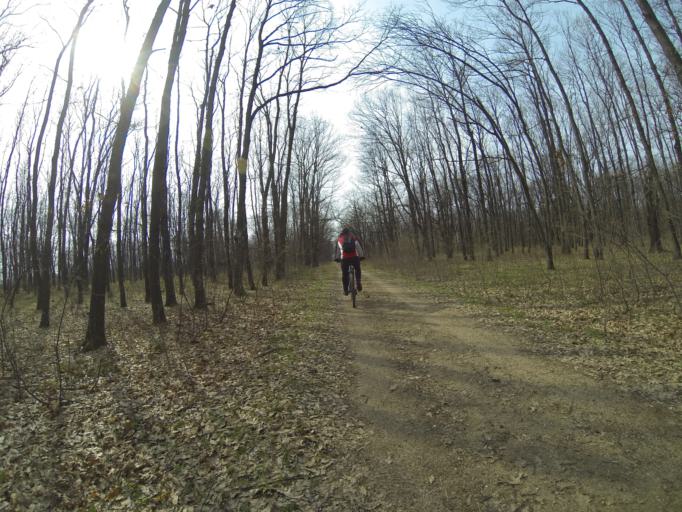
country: RO
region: Dolj
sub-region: Comuna Breasta
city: Breasta
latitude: 44.2768
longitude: 23.6898
